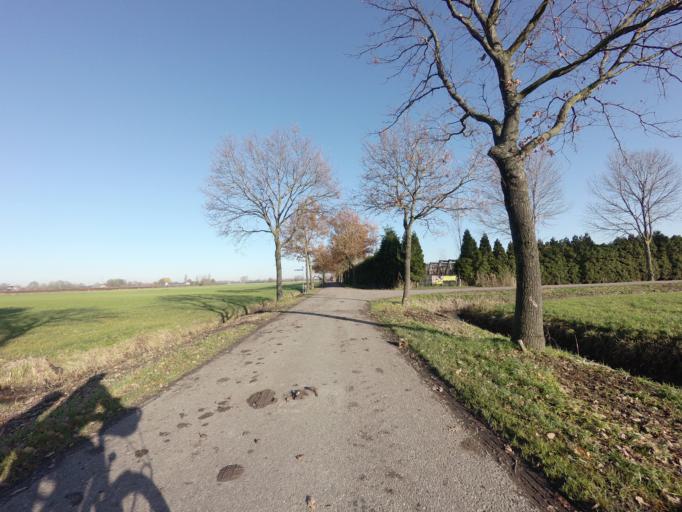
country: NL
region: Gelderland
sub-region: Gemeente Neerijnen
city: Neerijnen
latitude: 51.7917
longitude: 5.2969
